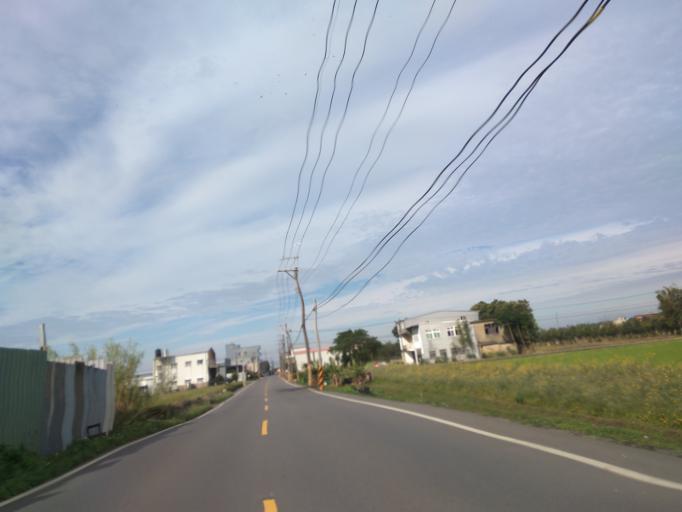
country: TW
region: Taiwan
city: Taoyuan City
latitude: 24.9508
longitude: 121.1353
